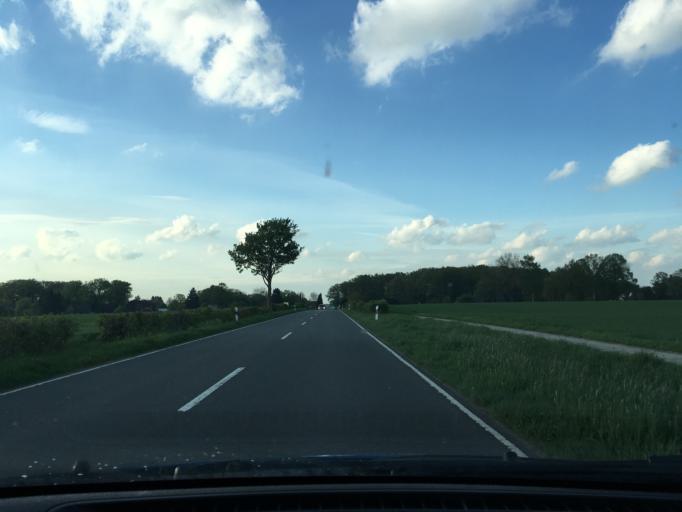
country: DE
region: Lower Saxony
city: Bergen
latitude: 52.8220
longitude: 9.9714
